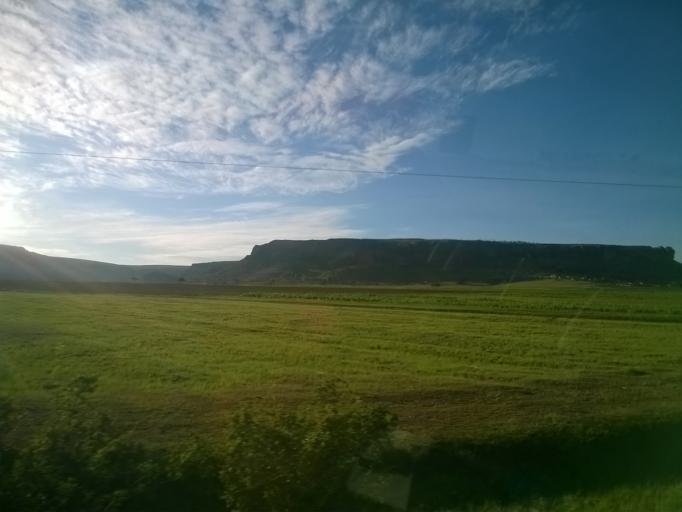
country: LS
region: Berea
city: Teyateyaneng
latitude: -29.1660
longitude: 27.6449
